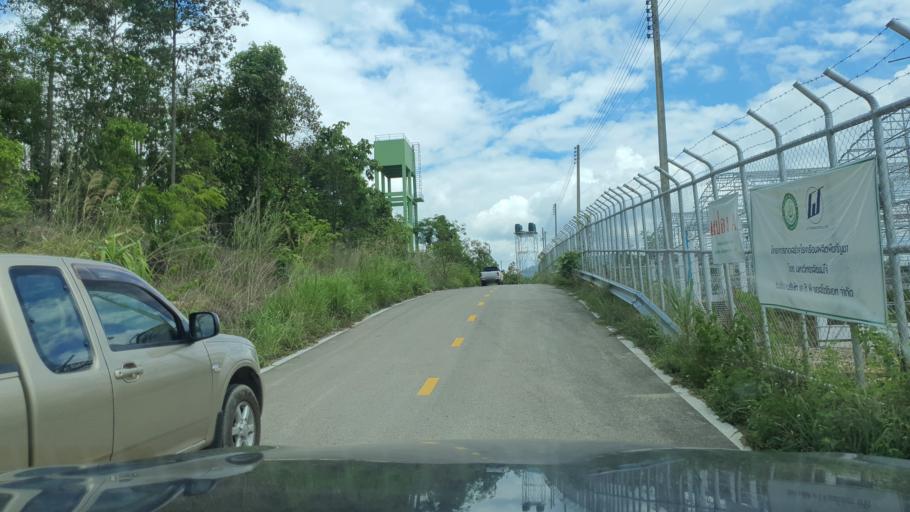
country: TH
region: Chiang Mai
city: San Sai
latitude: 18.9252
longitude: 99.0529
